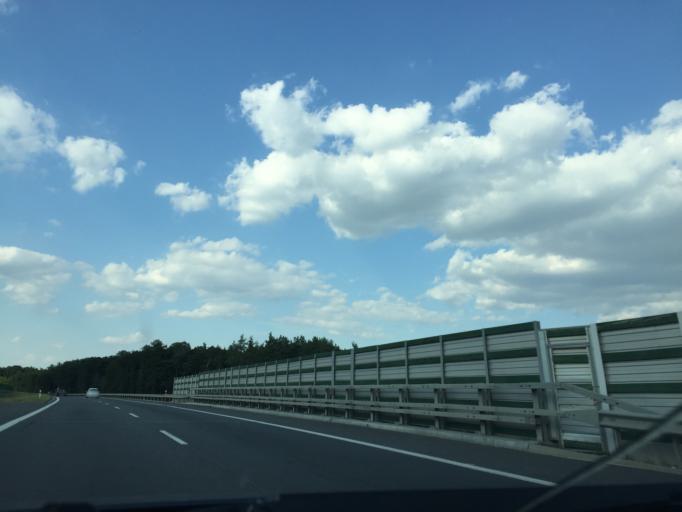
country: PL
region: Masovian Voivodeship
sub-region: Powiat szydlowiecki
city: Oronsko
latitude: 51.3145
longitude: 21.0141
